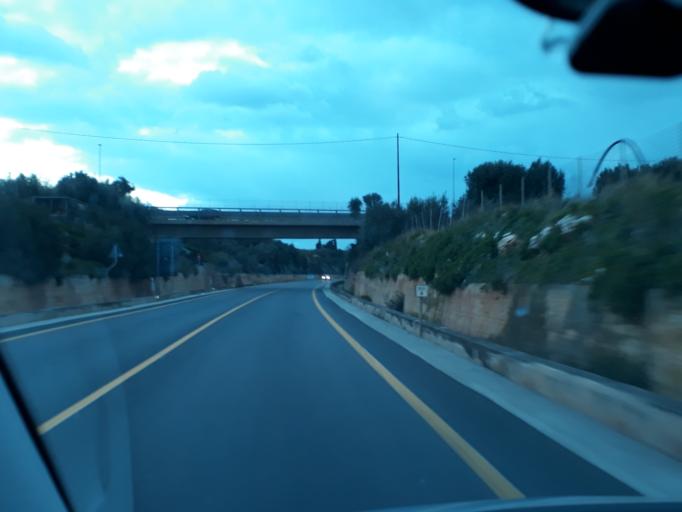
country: IT
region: Apulia
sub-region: Provincia di Brindisi
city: Fasano
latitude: 40.8336
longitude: 17.3501
